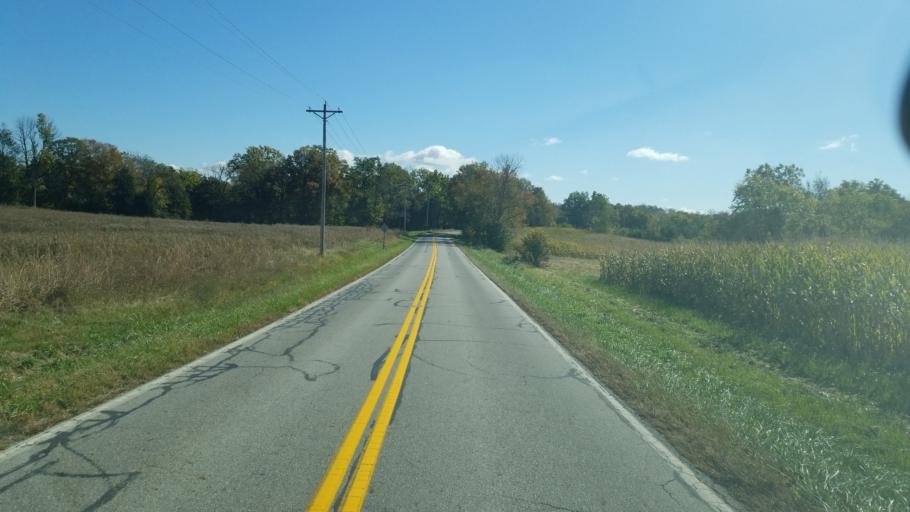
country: US
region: Ohio
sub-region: Highland County
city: Leesburg
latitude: 39.2753
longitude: -83.4864
